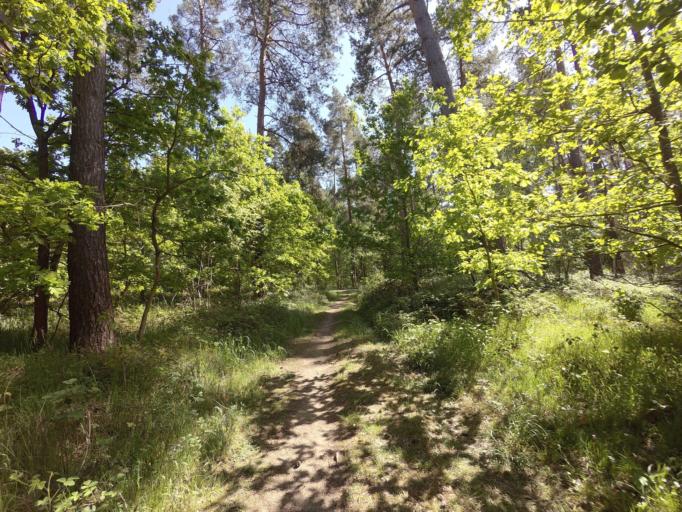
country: DE
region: Lower Saxony
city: Lehre
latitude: 52.3150
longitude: 10.6549
